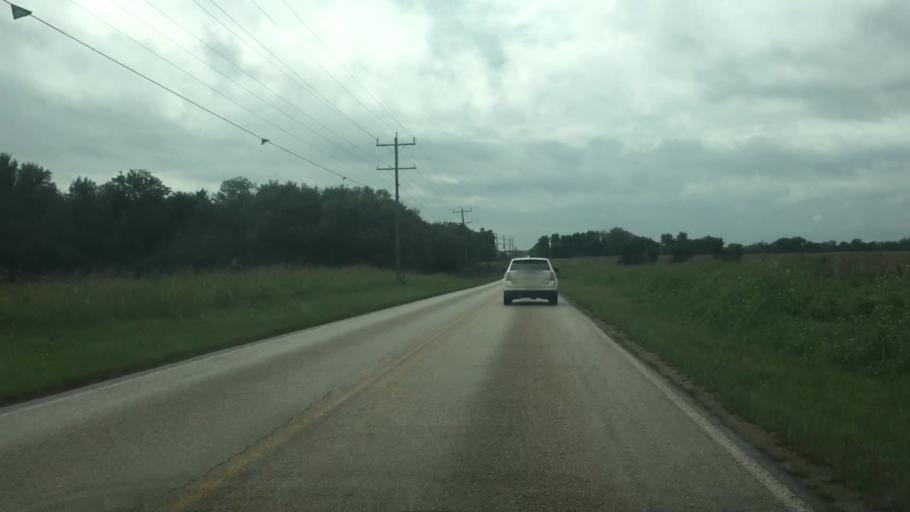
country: US
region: Kansas
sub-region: Allen County
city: Humboldt
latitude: 37.8432
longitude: -95.4369
